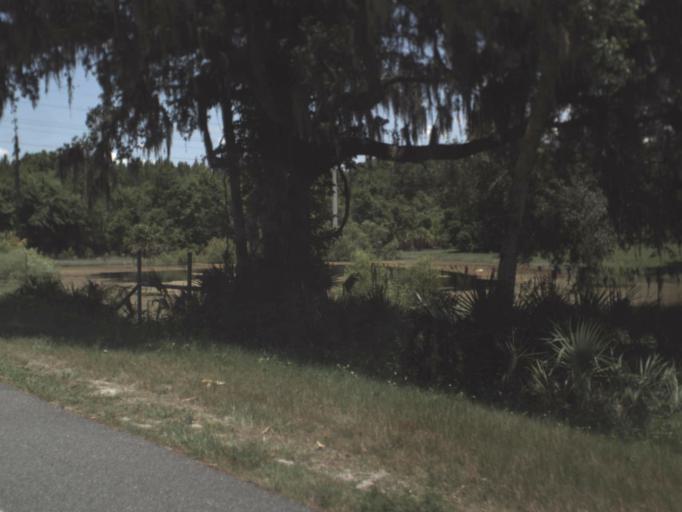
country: US
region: Florida
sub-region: Levy County
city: Manatee Road
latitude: 29.6120
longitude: -82.9829
